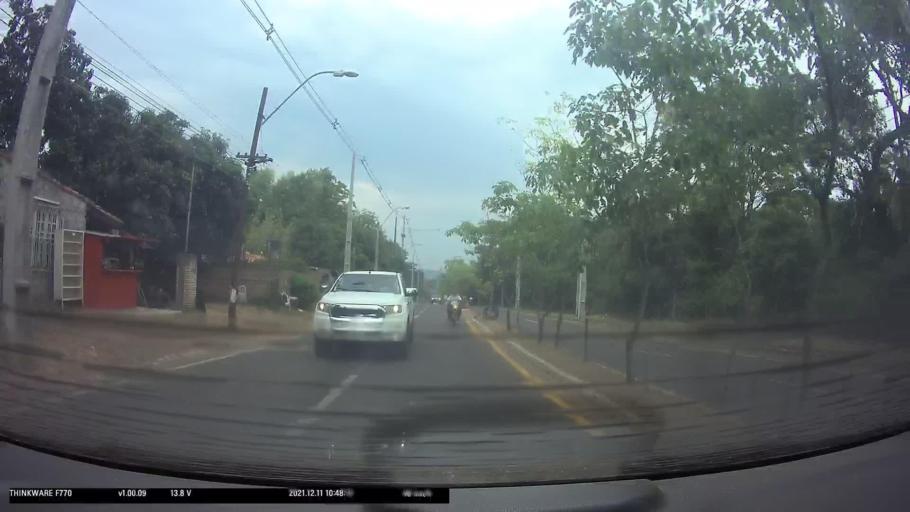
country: PY
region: Cordillera
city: San Bernardino
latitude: -25.3009
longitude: -57.2892
